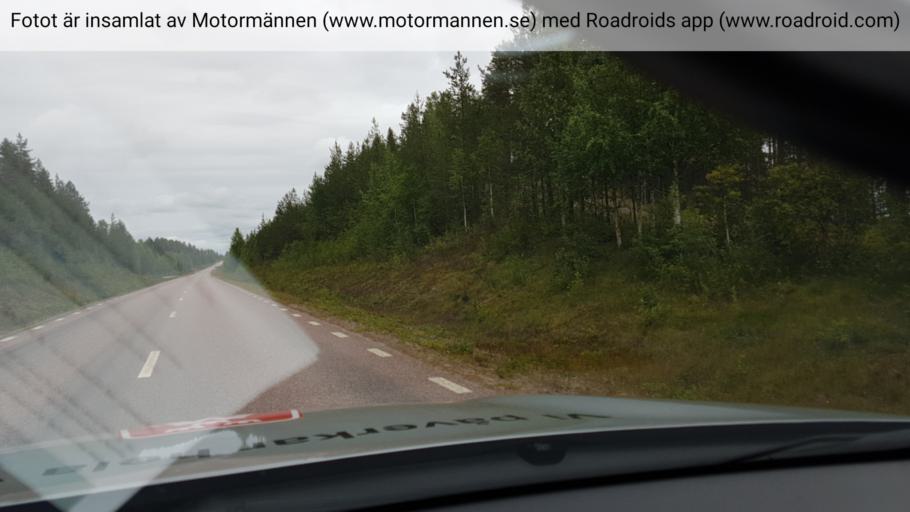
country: SE
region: Norrbotten
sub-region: Overkalix Kommun
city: OEverkalix
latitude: 67.0769
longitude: 22.5320
